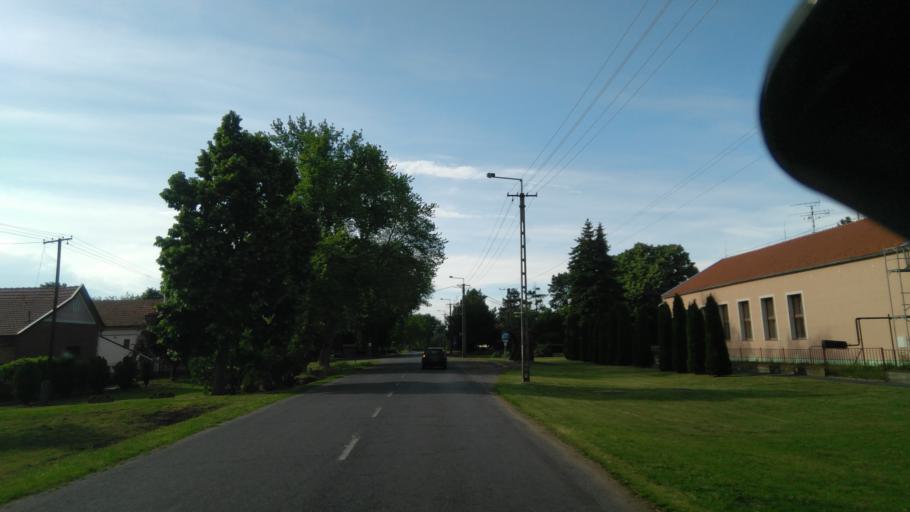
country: HU
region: Bekes
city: Lokoshaza
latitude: 46.4267
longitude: 21.2312
